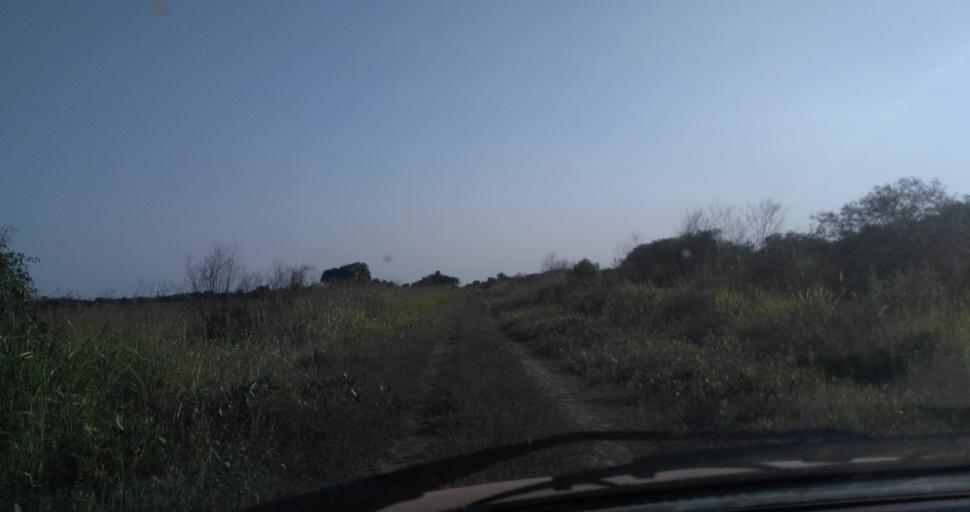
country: AR
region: Chaco
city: Fontana
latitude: -27.4294
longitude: -59.0585
